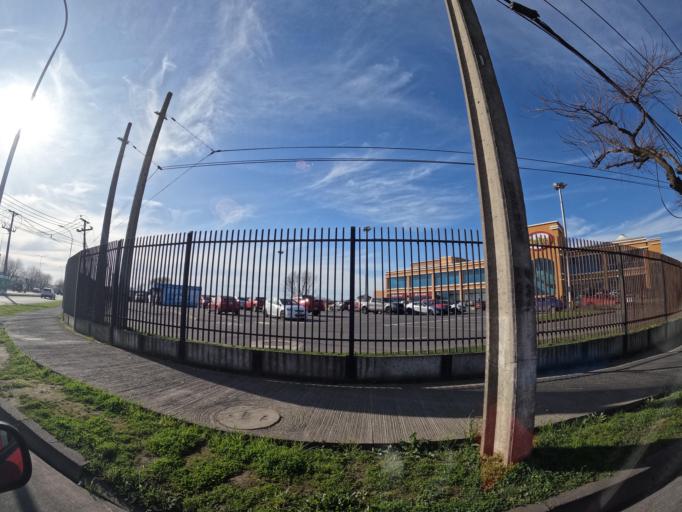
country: CL
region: Biobio
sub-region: Provincia de Concepcion
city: Concepcion
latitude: -36.7783
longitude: -73.0779
